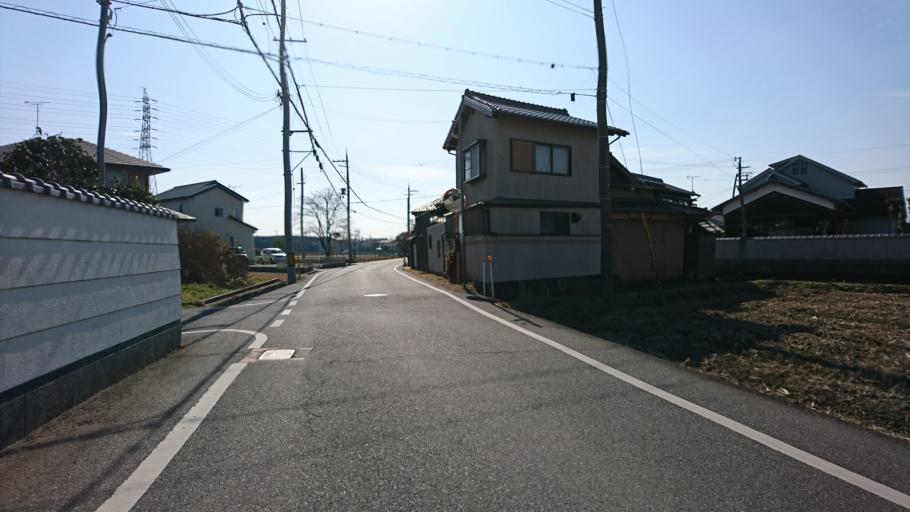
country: JP
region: Hyogo
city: Kakogawacho-honmachi
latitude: 34.7904
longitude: 134.8312
